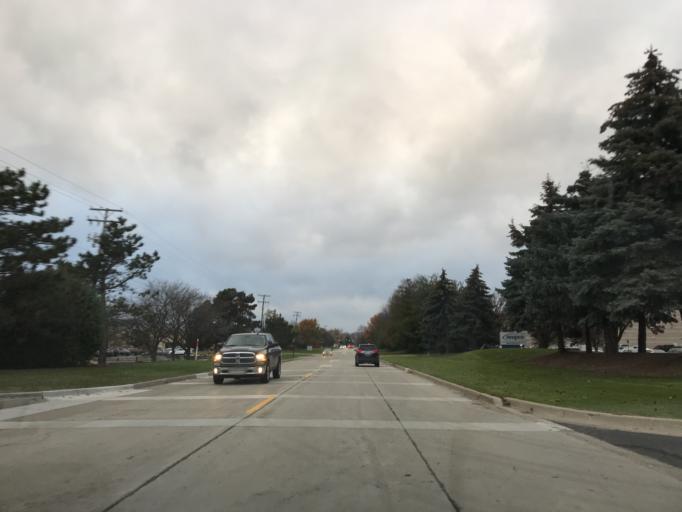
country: US
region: Michigan
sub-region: Oakland County
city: Novi
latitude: 42.4901
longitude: -83.4296
